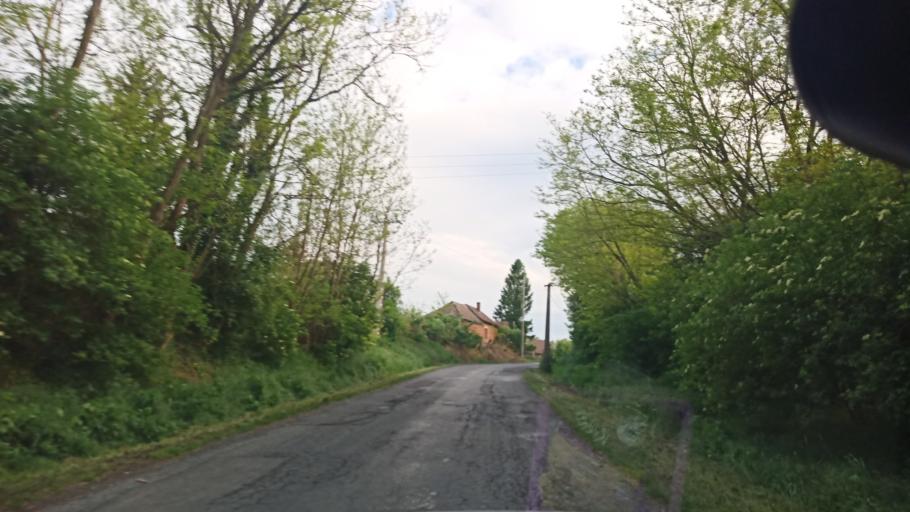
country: HU
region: Zala
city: Pacsa
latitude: 46.7294
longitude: 17.0036
